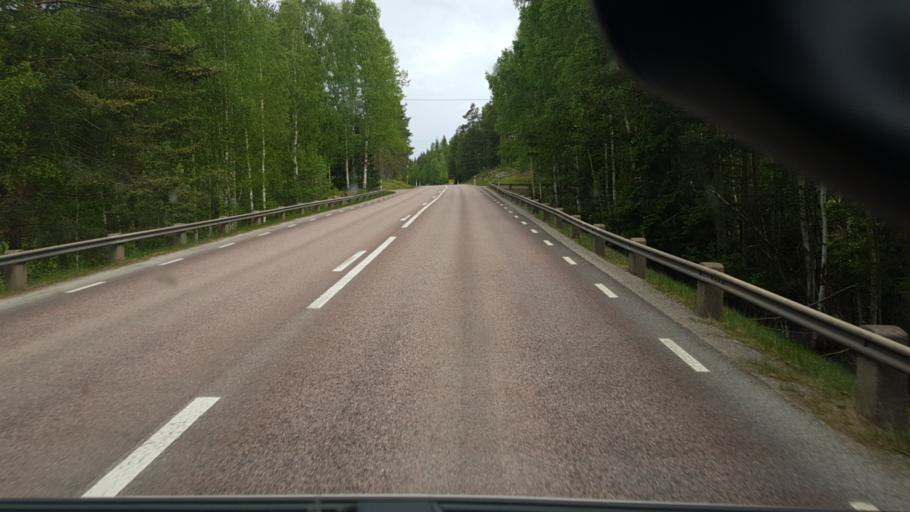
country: SE
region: Vaermland
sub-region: Arvika Kommun
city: Arvika
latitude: 59.5925
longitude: 12.6449
